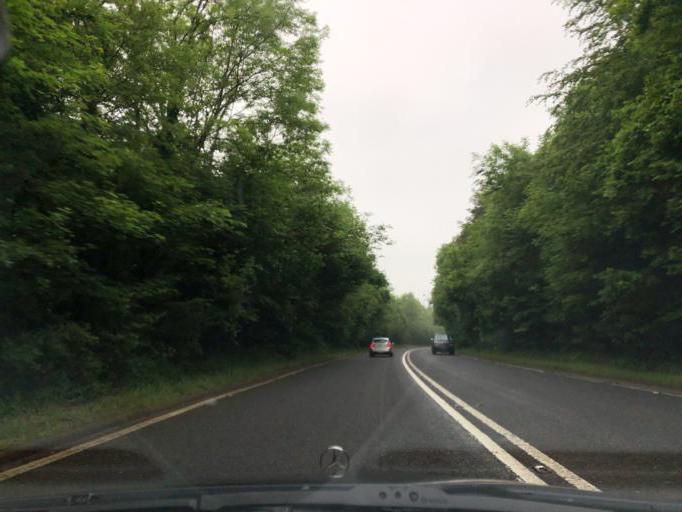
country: GB
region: England
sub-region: Warwickshire
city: Harbury
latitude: 52.2089
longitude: -1.5015
